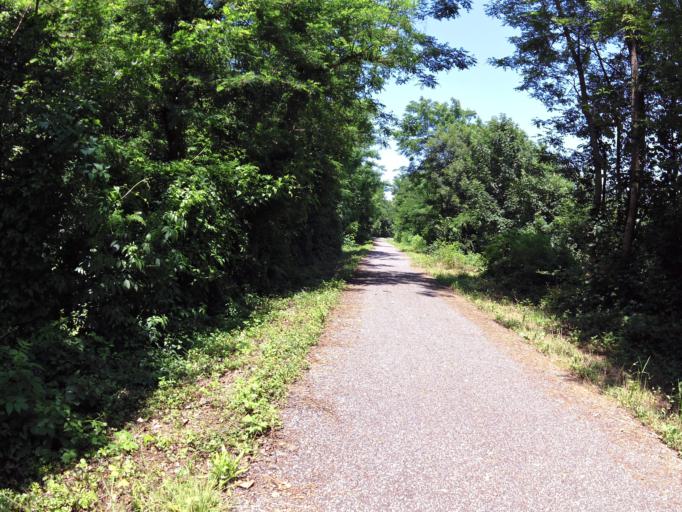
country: FR
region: Aquitaine
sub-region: Departement des Pyrenees-Atlantiques
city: Salies-de-Bearn
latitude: 43.4466
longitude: -0.9939
